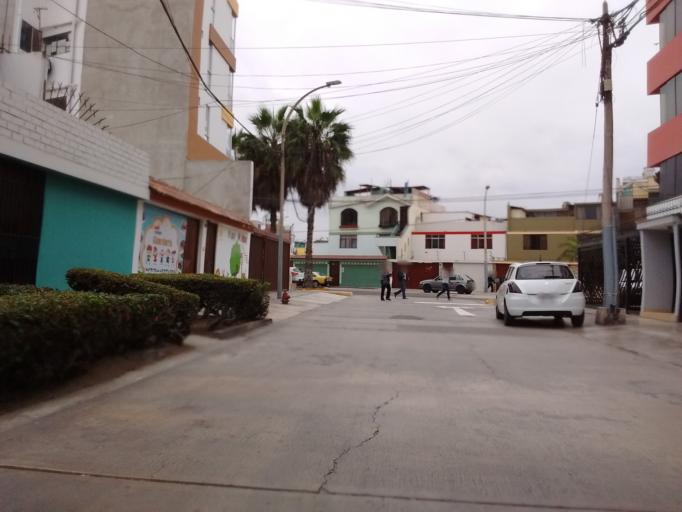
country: PE
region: Callao
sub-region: Callao
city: Callao
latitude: -12.0654
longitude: -77.0966
